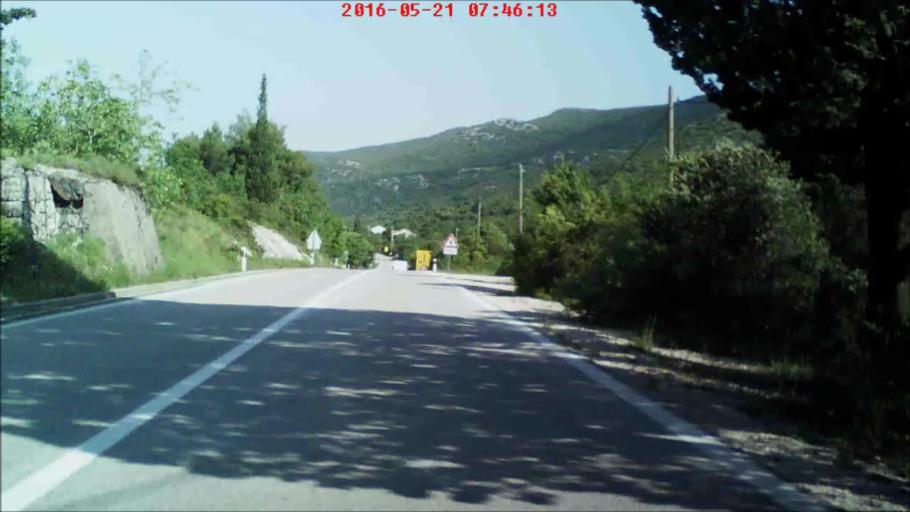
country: HR
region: Dubrovacko-Neretvanska
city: Ston
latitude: 42.8278
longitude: 17.7548
